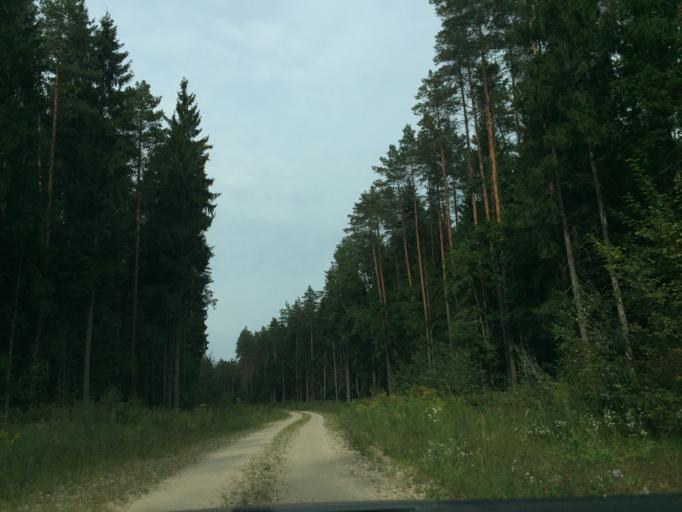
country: LV
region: Baldone
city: Baldone
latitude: 56.7479
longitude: 24.4650
